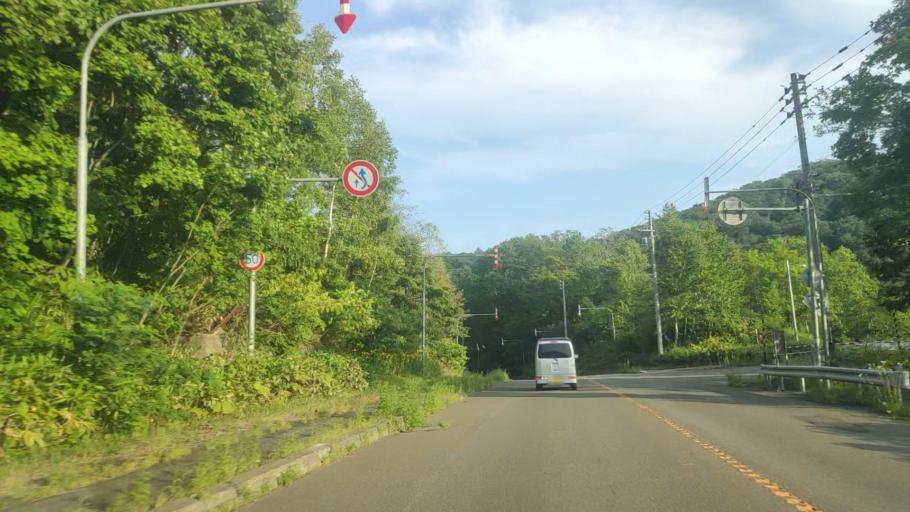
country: JP
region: Hokkaido
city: Iwamizawa
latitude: 43.0174
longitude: 141.9939
